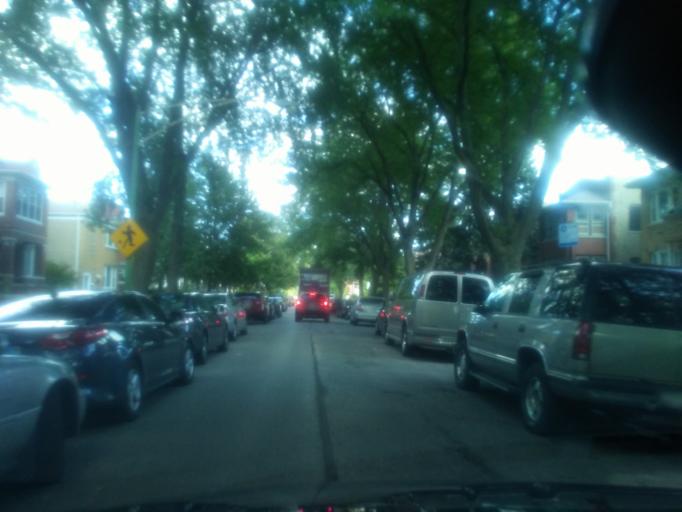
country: US
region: Illinois
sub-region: Cook County
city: Harwood Heights
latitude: 41.9588
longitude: -87.7596
